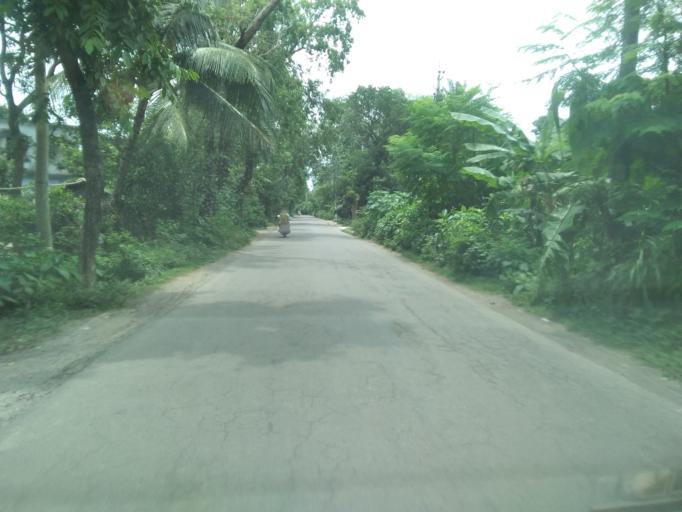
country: IN
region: West Bengal
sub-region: North 24 Parganas
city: Taki
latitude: 22.5609
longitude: 89.0044
